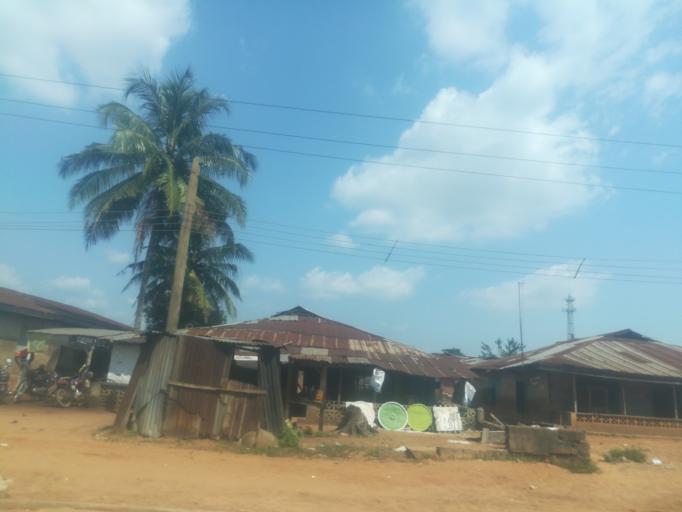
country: NG
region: Oyo
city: Moniya
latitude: 7.5051
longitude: 3.9129
